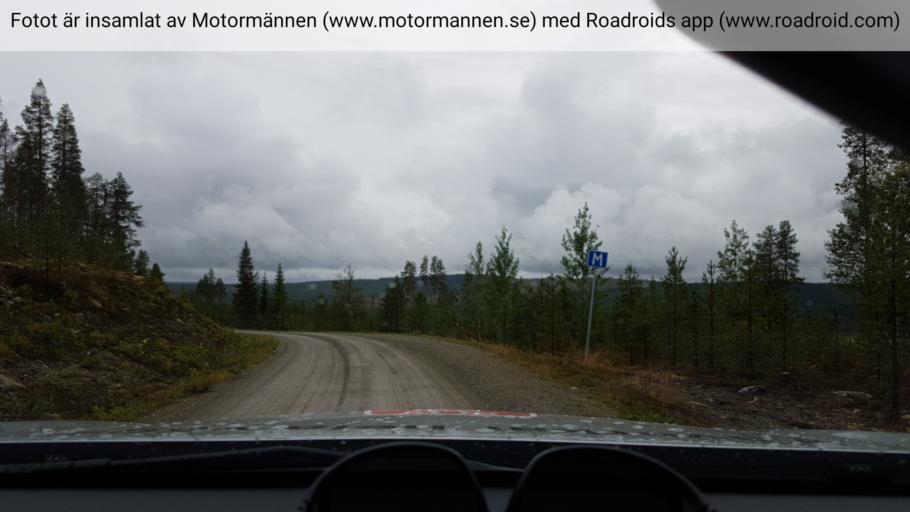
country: SE
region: Vaesterbotten
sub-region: Storumans Kommun
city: Storuman
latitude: 64.8354
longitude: 17.4034
